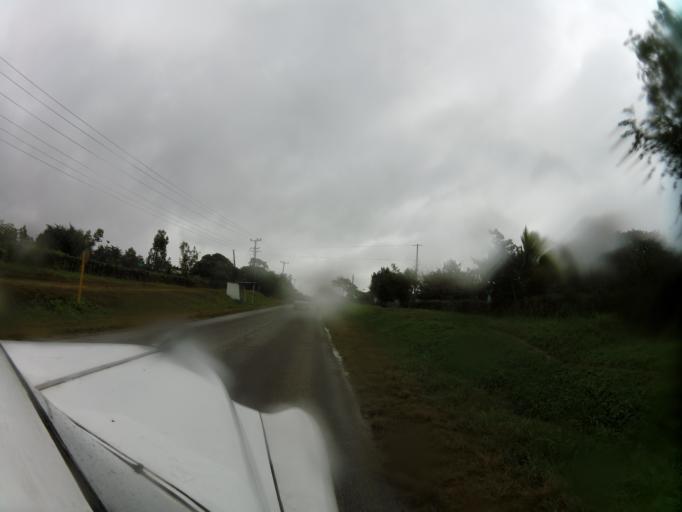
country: CU
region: Las Tunas
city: Las Tunas
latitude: 20.9187
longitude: -76.8821
